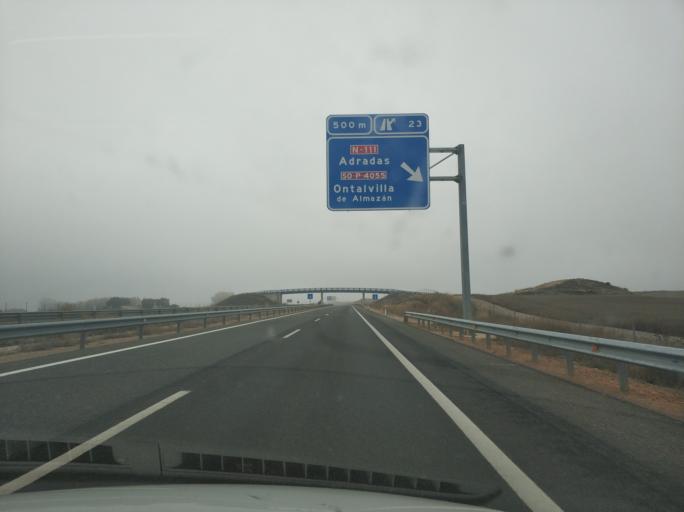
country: ES
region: Castille and Leon
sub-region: Provincia de Soria
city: Adradas
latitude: 41.3581
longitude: -2.4751
